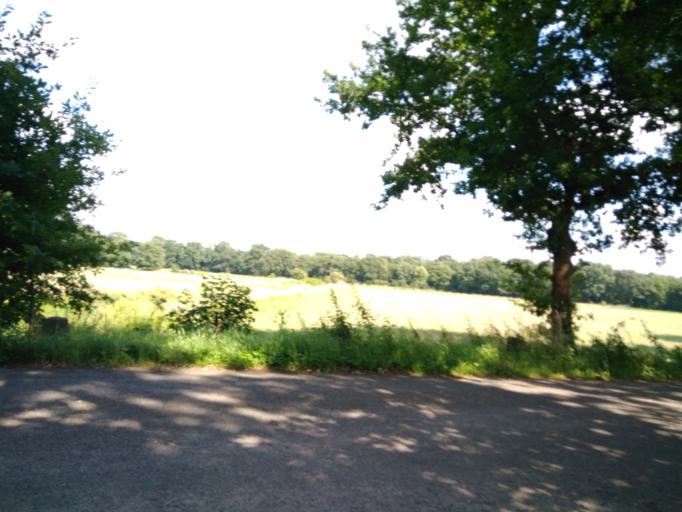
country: DE
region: North Rhine-Westphalia
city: Dorsten
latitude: 51.6795
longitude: 6.9758
